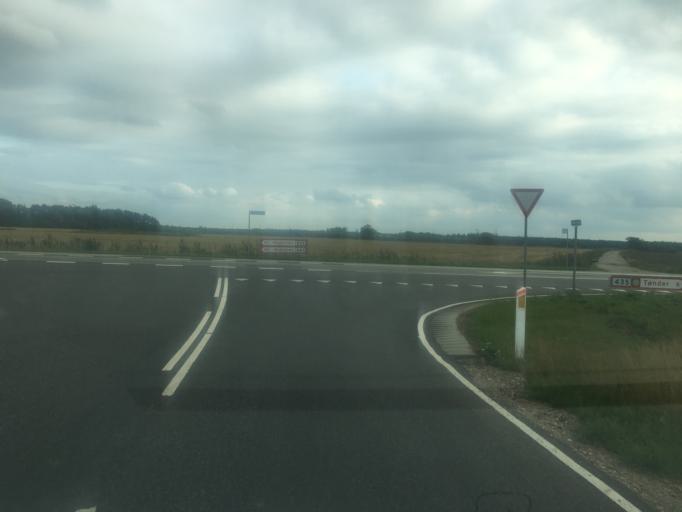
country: DE
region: Schleswig-Holstein
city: Ellhoft
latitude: 54.9661
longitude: 8.9482
